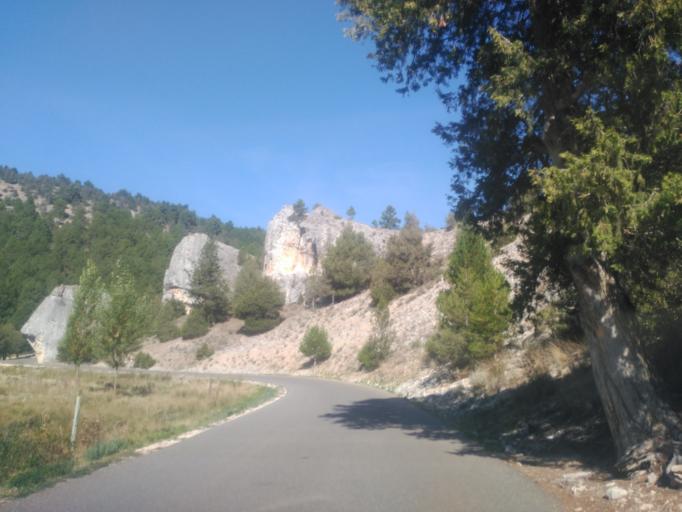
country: ES
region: Castille and Leon
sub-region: Provincia de Soria
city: Ucero
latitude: 41.7408
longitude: -3.0581
